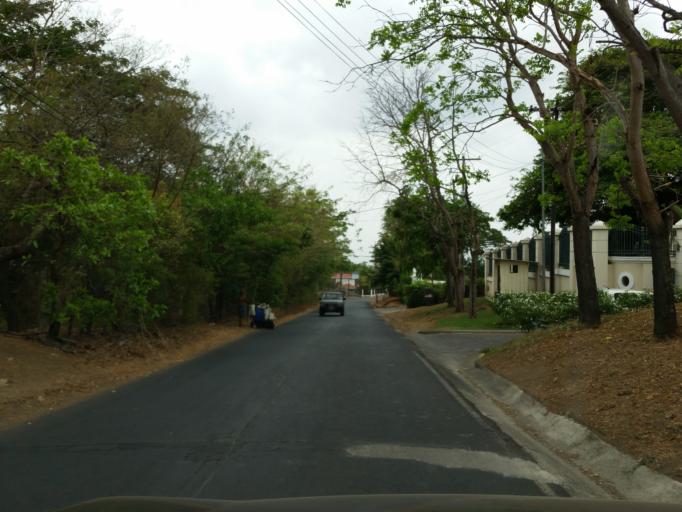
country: NI
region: Managua
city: Managua
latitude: 12.0920
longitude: -86.2662
